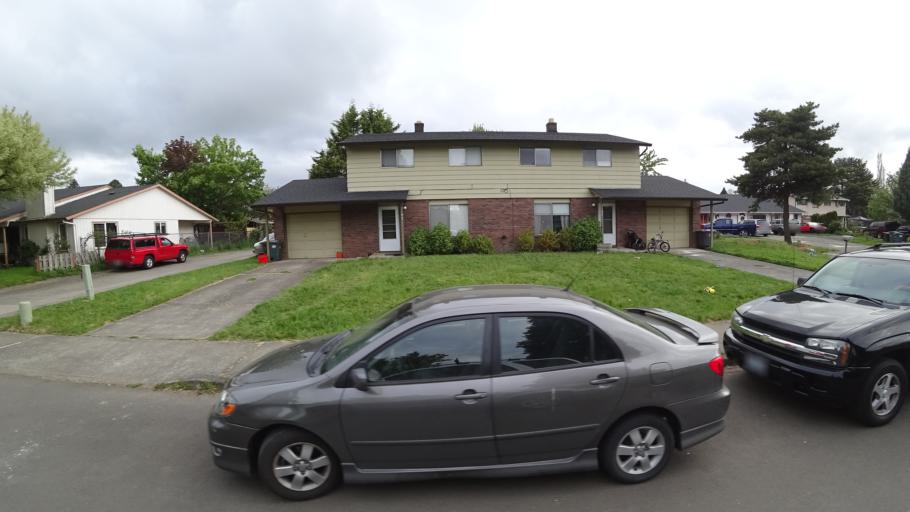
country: US
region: Oregon
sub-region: Washington County
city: Hillsboro
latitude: 45.5325
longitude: -122.9598
